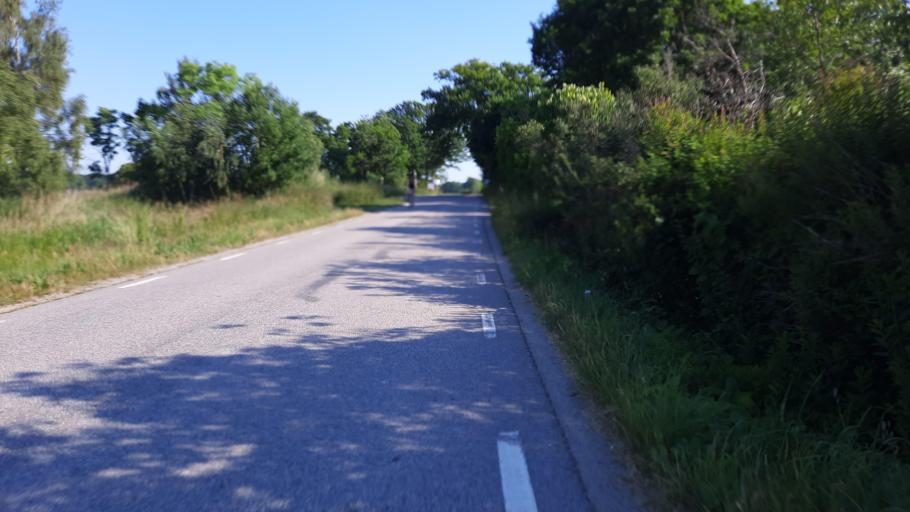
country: SE
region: Blekinge
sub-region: Karlskrona Kommun
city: Sturko
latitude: 56.1023
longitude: 15.6906
